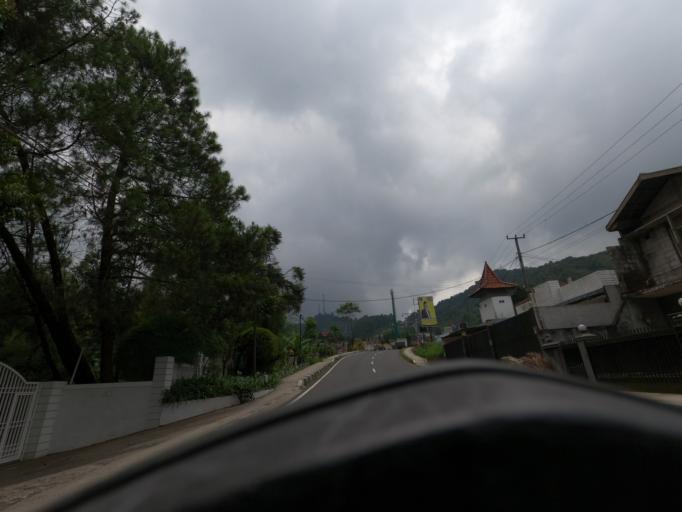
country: ID
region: West Java
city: Caringin
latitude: -6.7107
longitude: 106.9989
